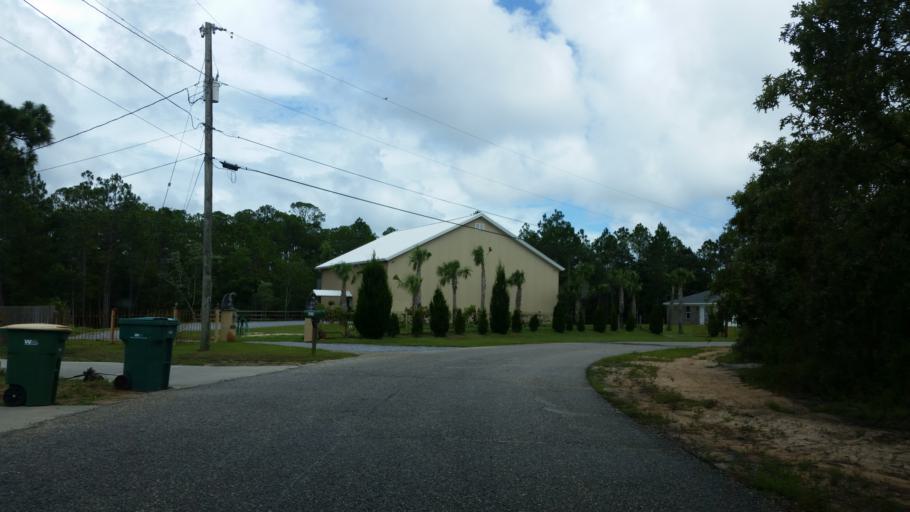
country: US
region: Florida
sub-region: Santa Rosa County
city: Navarre
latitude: 30.4324
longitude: -86.8517
